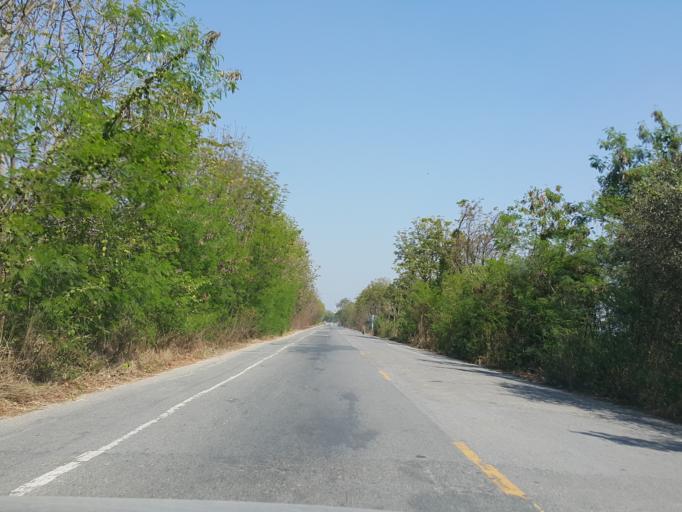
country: TH
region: Chiang Mai
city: San Kamphaeng
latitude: 18.7283
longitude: 99.1087
